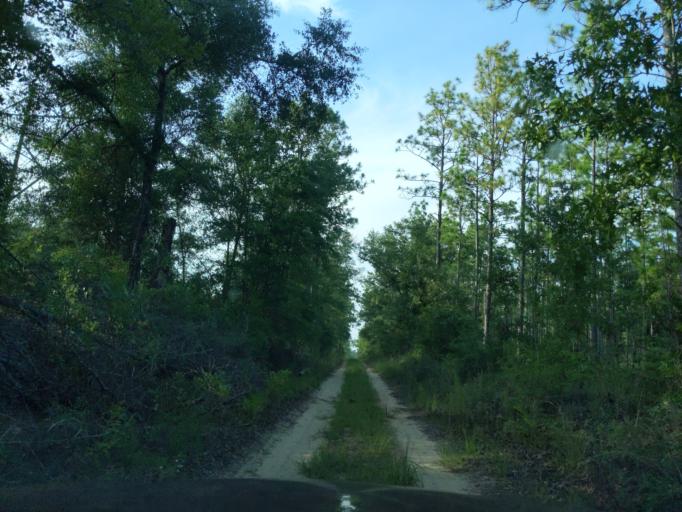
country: US
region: Florida
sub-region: Leon County
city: Tallahassee
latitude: 30.3610
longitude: -84.3610
